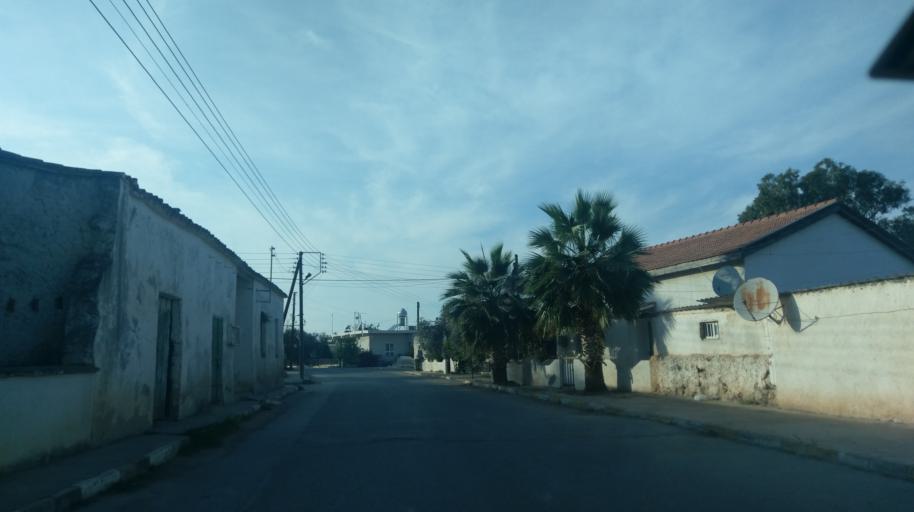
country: CY
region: Ammochostos
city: Achna
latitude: 35.0976
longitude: 33.7941
